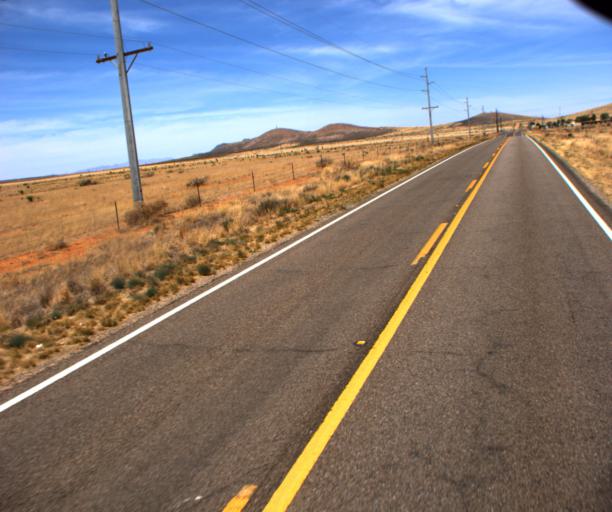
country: US
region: Arizona
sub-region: Cochise County
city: Willcox
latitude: 31.8788
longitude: -109.6951
